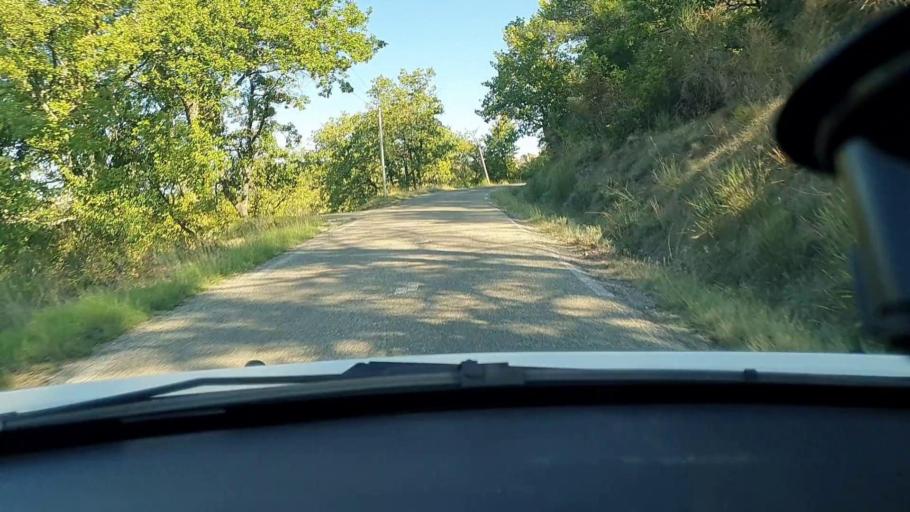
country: FR
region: Languedoc-Roussillon
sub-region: Departement du Gard
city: Saint-Julien-de-Peyrolas
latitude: 44.2565
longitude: 4.5239
